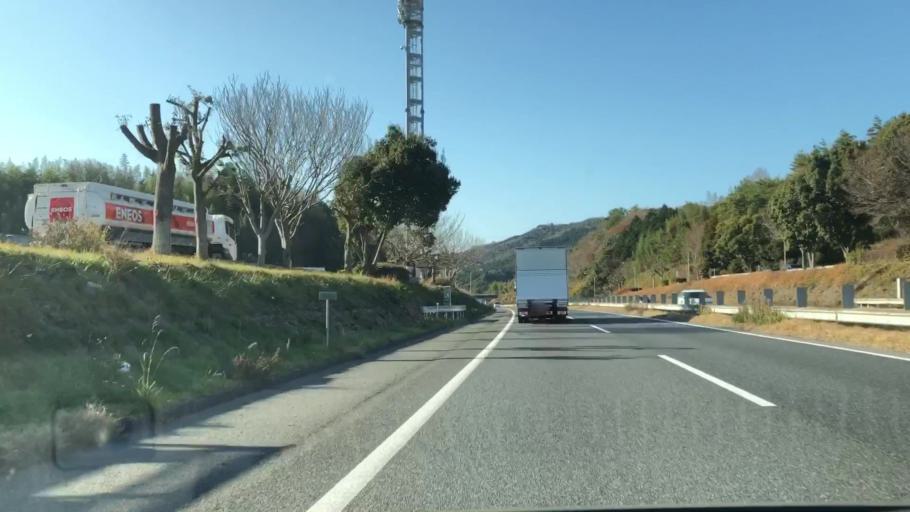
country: JP
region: Yamaguchi
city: Kudamatsu
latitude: 34.0416
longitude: 131.9162
